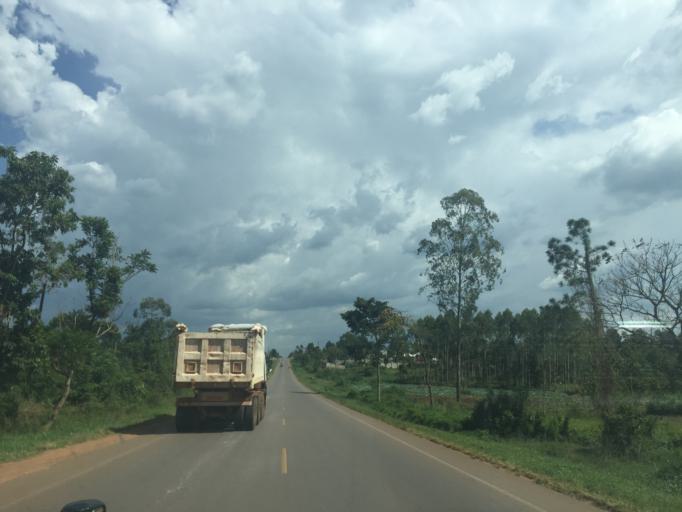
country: UG
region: Central Region
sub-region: Luwero District
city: Wobulenzi
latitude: 0.7379
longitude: 32.5198
